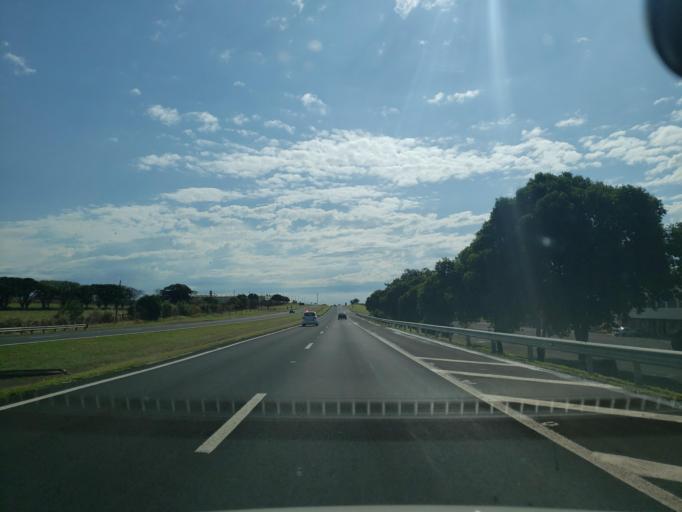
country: BR
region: Sao Paulo
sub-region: Pirajui
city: Pirajui
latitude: -22.0090
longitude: -49.4227
